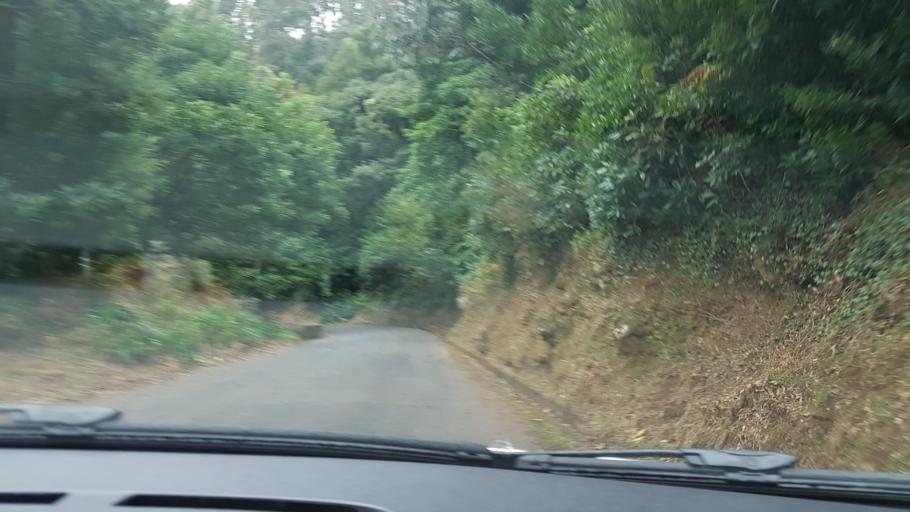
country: PT
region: Madeira
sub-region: Santa Cruz
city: Santa Cruz
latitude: 32.7274
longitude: -16.8148
